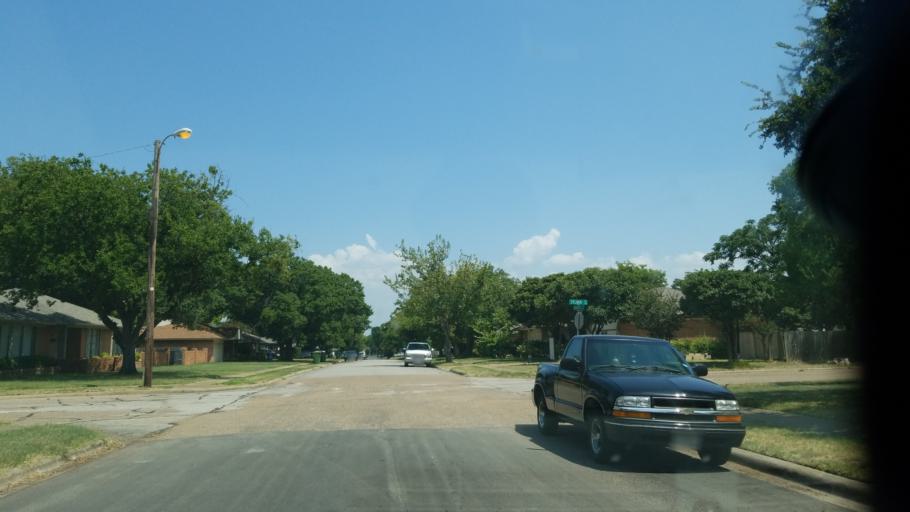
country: US
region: Texas
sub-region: Dallas County
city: Garland
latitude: 32.9287
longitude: -96.6438
